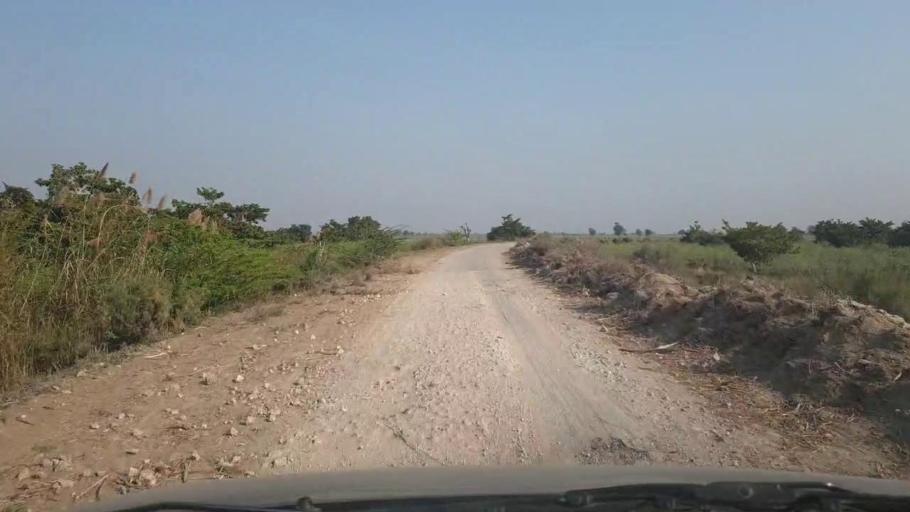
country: PK
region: Sindh
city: Digri
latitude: 25.2620
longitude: 69.1851
